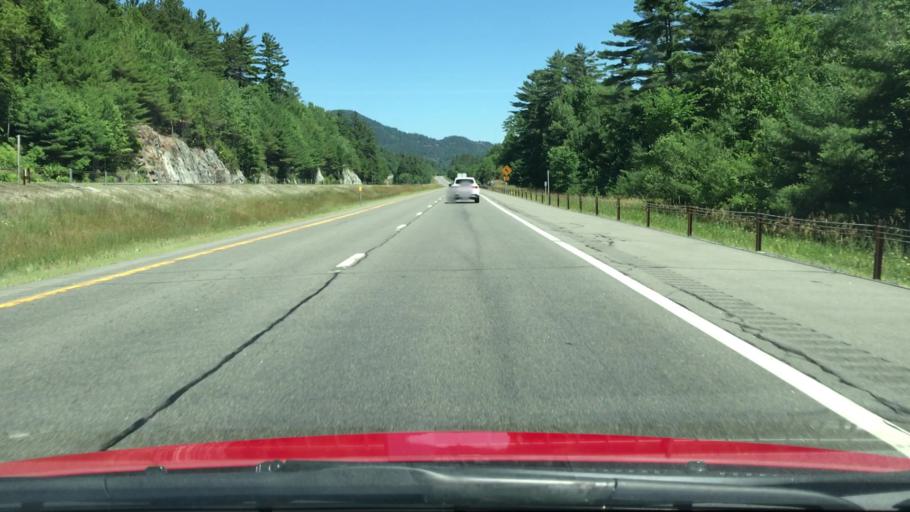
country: US
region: New York
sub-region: Essex County
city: Mineville
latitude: 43.9651
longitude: -73.7271
